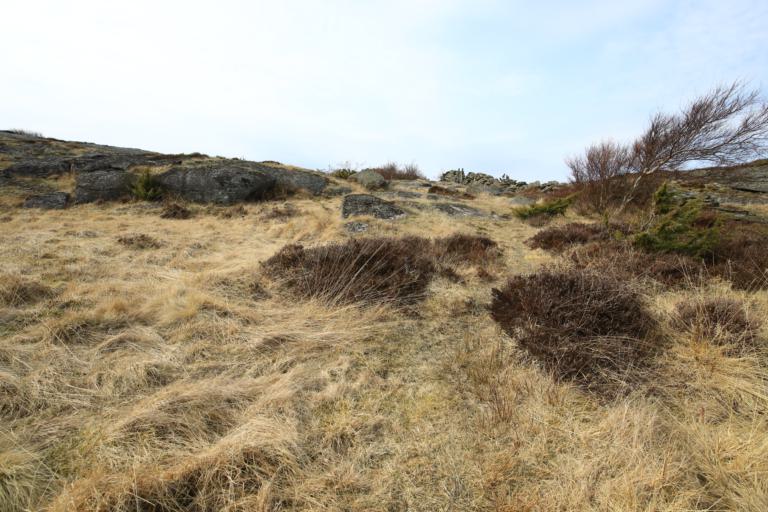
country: SE
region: Halland
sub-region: Kungsbacka Kommun
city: Frillesas
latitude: 57.2544
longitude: 12.0949
